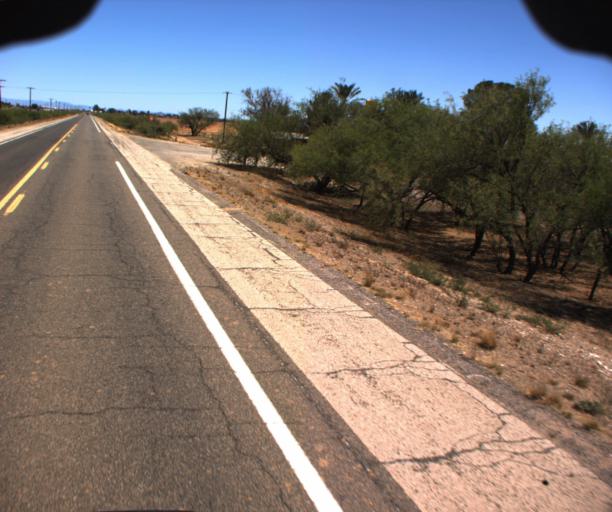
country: US
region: Arizona
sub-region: Yavapai County
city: Congress
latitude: 33.9388
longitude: -113.1939
